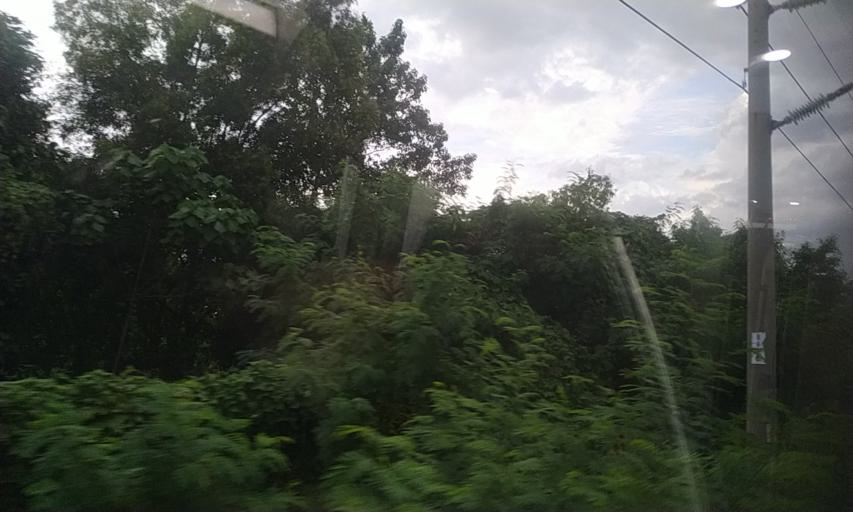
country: MY
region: Kuala Lumpur
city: Kuala Lumpur
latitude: 3.2257
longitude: 101.6727
